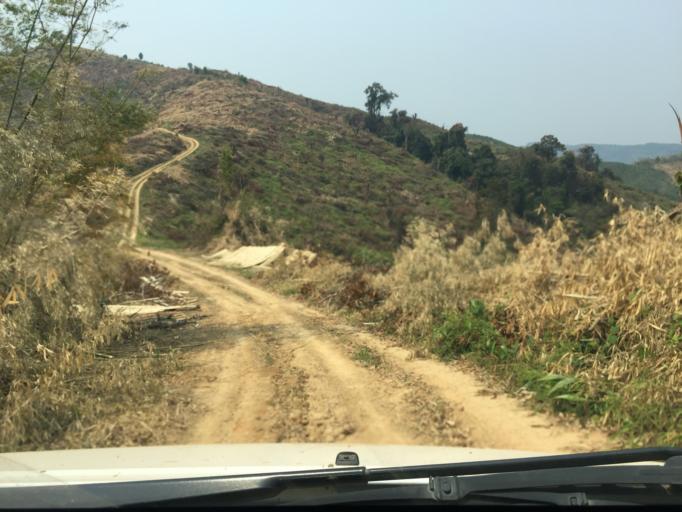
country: LA
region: Loungnamtha
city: Muang Nale
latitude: 20.6205
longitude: 101.6156
